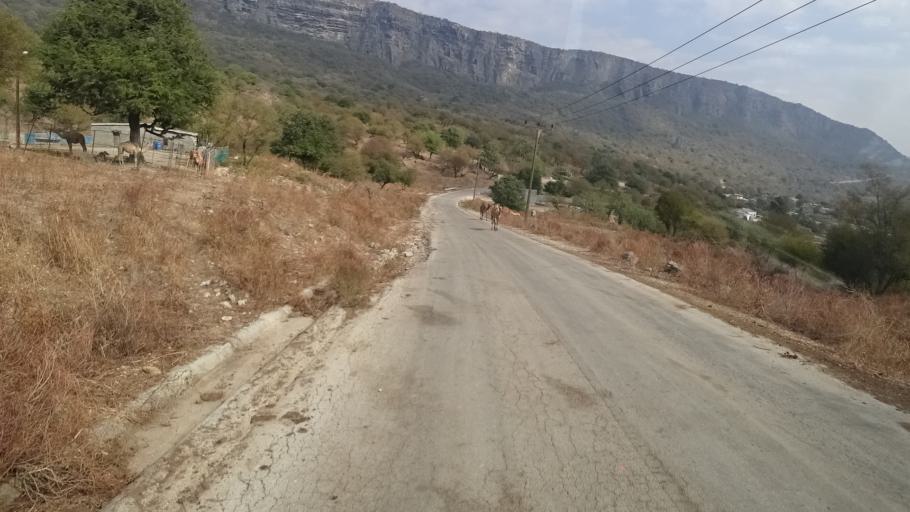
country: YE
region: Al Mahrah
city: Hawf
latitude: 16.7120
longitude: 53.2479
